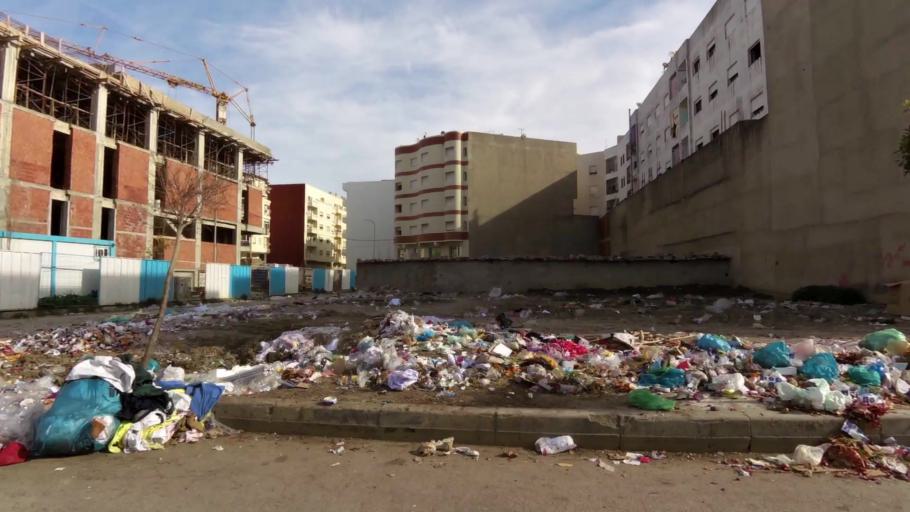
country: MA
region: Tanger-Tetouan
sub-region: Tanger-Assilah
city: Tangier
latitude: 35.7400
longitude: -5.7988
